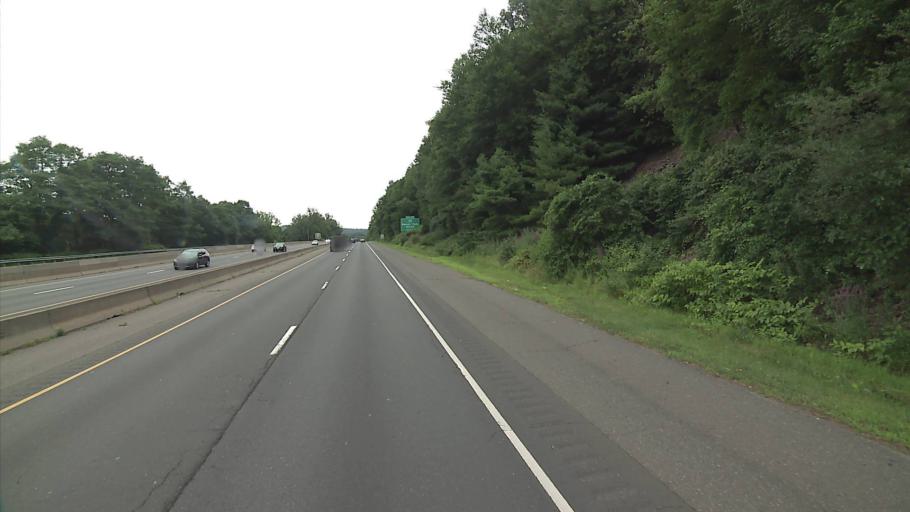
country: US
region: Connecticut
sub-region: New Haven County
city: Seymour
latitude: 41.4180
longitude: -73.0699
